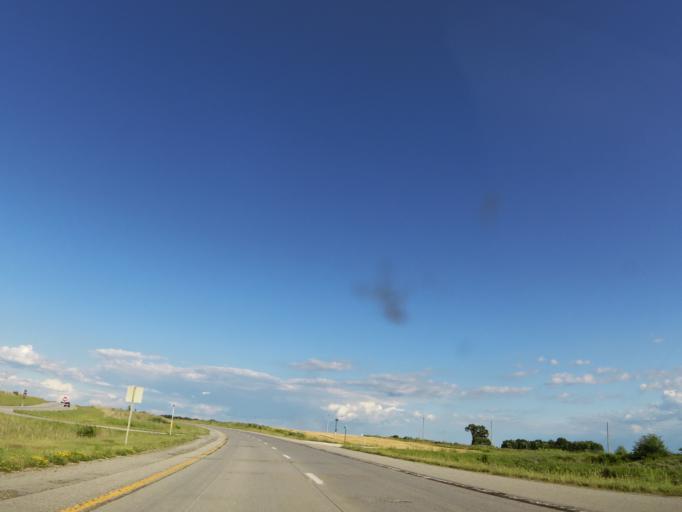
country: US
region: Missouri
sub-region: Pike County
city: Bowling Green
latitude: 39.2615
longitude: -91.0709
